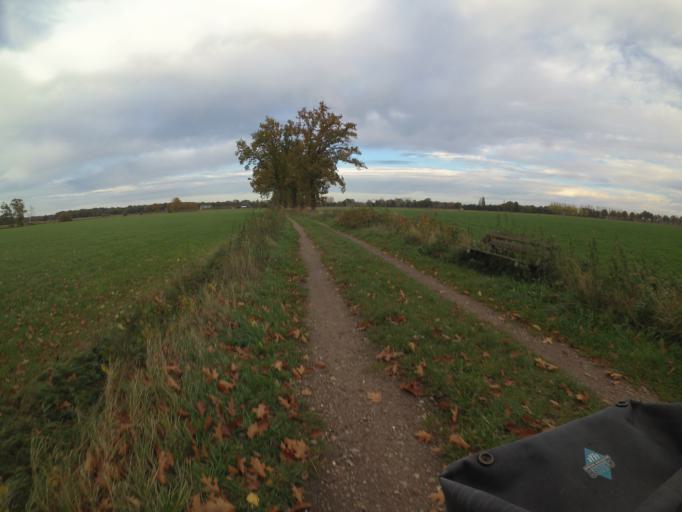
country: NL
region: North Brabant
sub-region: Gemeente Haaren
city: Haaren
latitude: 51.6145
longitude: 5.2616
